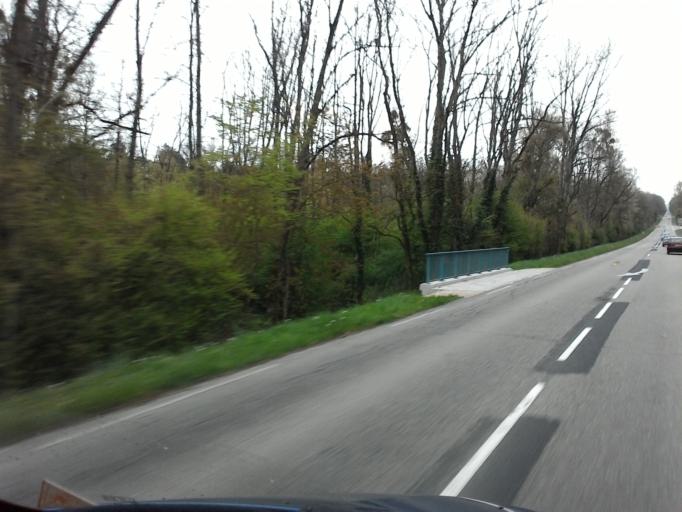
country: FR
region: Lorraine
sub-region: Departement de Meurthe-et-Moselle
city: Domgermain
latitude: 48.6427
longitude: 5.8656
